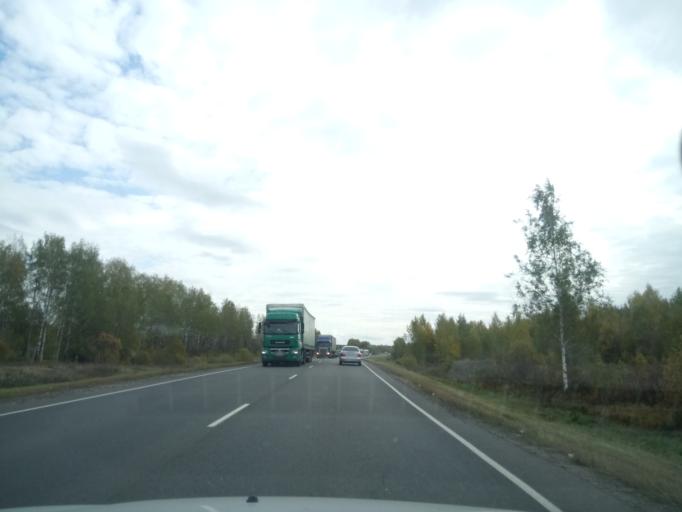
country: RU
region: Nizjnij Novgorod
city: Lukoyanov
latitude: 55.0597
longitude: 44.3630
